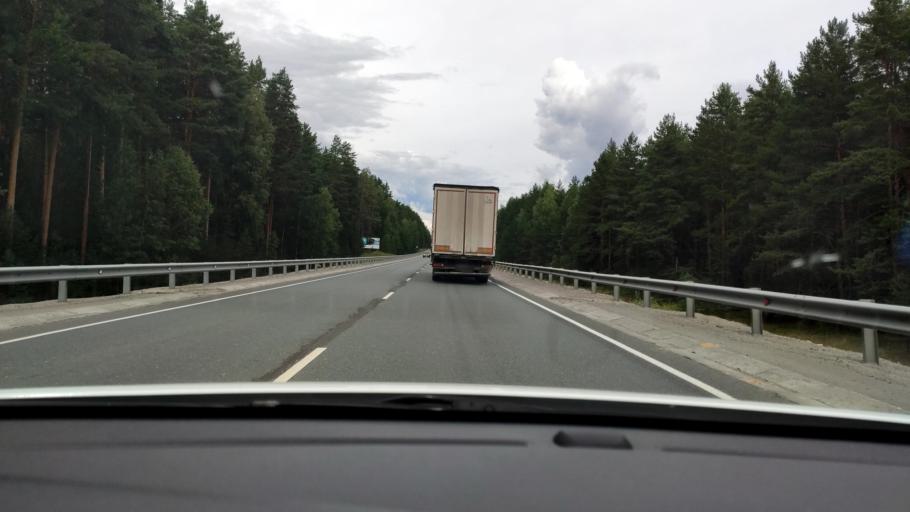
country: RU
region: Mariy-El
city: Pomary
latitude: 56.0137
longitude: 48.3797
